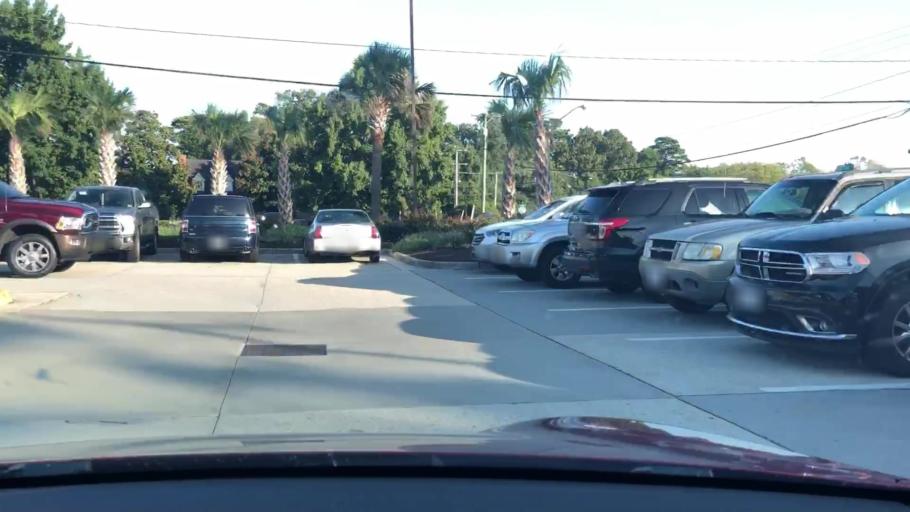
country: US
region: Virginia
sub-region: City of Virginia Beach
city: Virginia Beach
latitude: 36.8472
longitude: -76.0361
